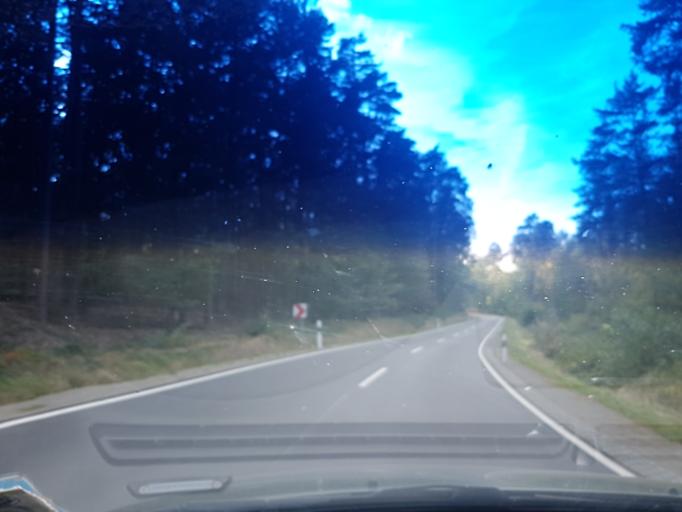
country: DE
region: Bavaria
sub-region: Regierungsbezirk Mittelfranken
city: Wachenroth
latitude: 49.7348
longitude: 10.6874
